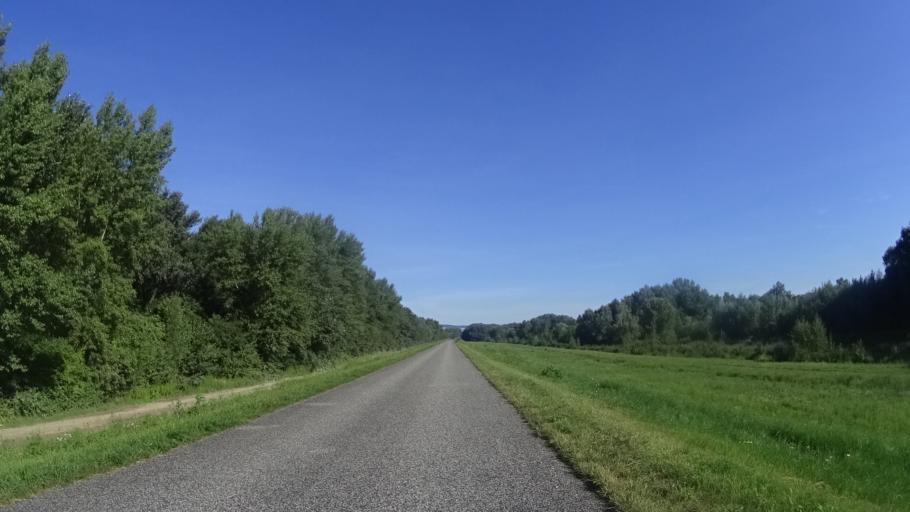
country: SK
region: Bratislavsky
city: Bratislava
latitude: 48.0912
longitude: 17.1537
